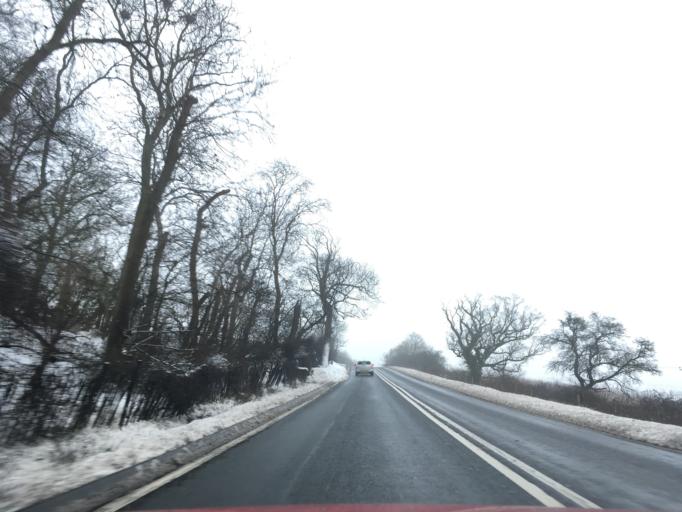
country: GB
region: England
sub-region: Warwickshire
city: Stratford-upon-Avon
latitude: 52.2000
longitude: -1.7680
